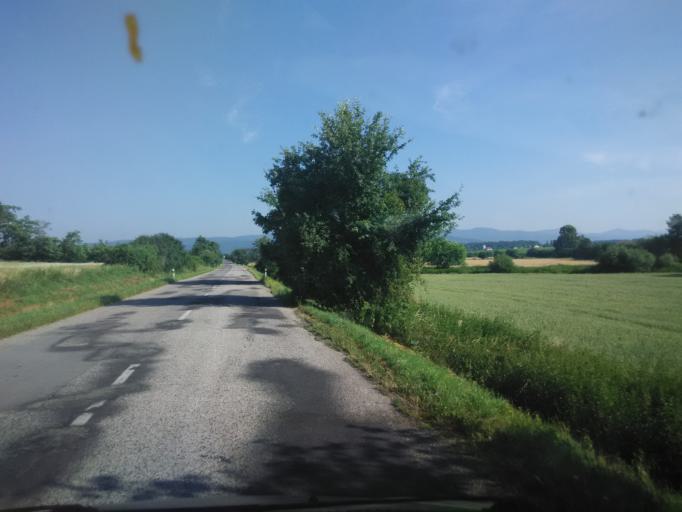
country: SK
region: Nitriansky
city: Levice
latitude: 48.2741
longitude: 18.6980
